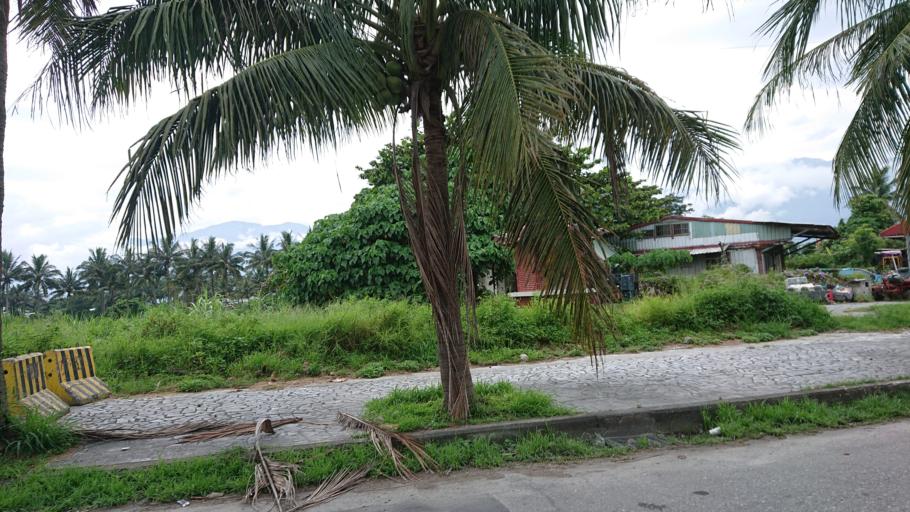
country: TW
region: Taiwan
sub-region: Hualien
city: Hualian
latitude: 23.9698
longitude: 121.6108
